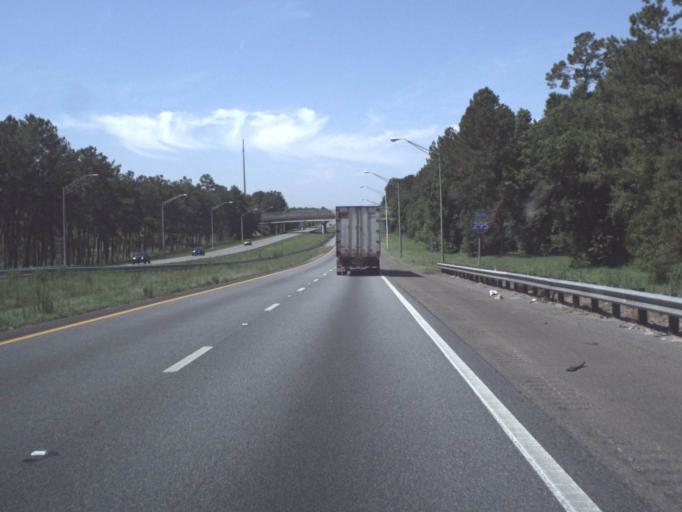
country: US
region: Florida
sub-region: Nassau County
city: Nassau Village-Ratliff
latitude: 30.4055
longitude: -81.7537
